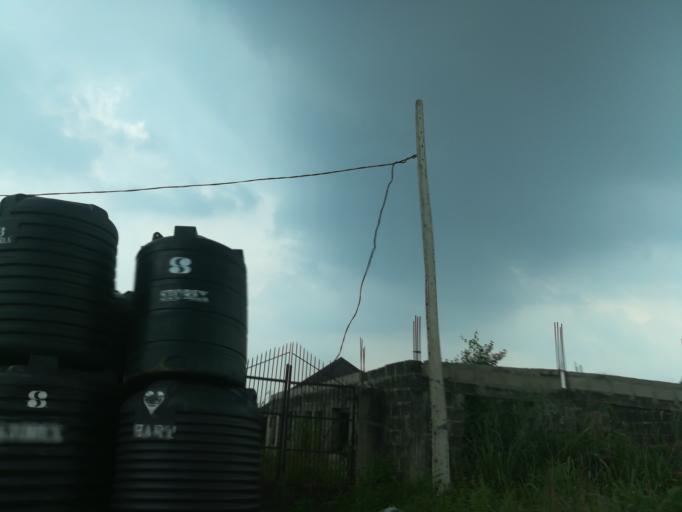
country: NG
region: Lagos
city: Ikorodu
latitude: 6.5859
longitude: 3.5868
